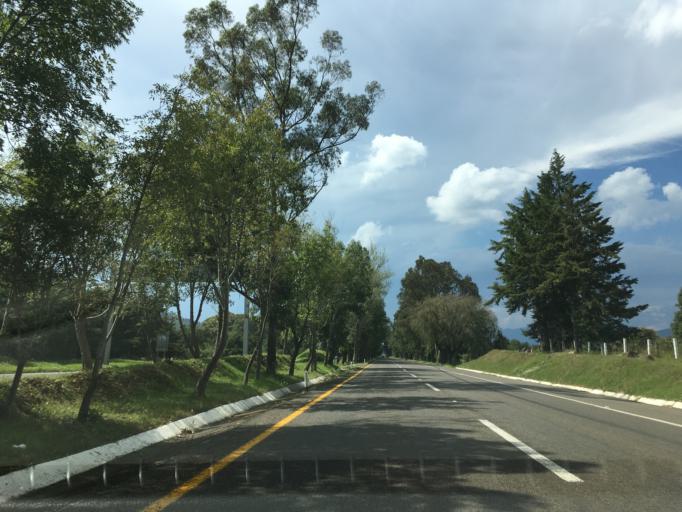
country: MX
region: Michoacan
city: Patzcuaro
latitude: 19.5346
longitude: -101.5692
